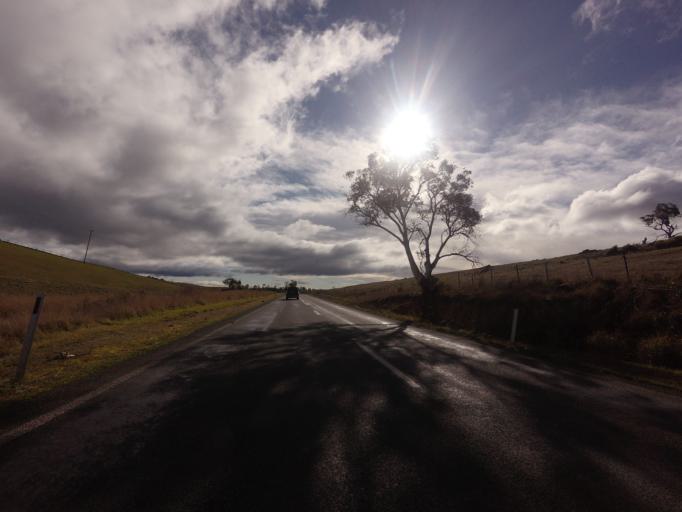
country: AU
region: Tasmania
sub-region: Derwent Valley
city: New Norfolk
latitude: -42.5971
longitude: 146.8853
